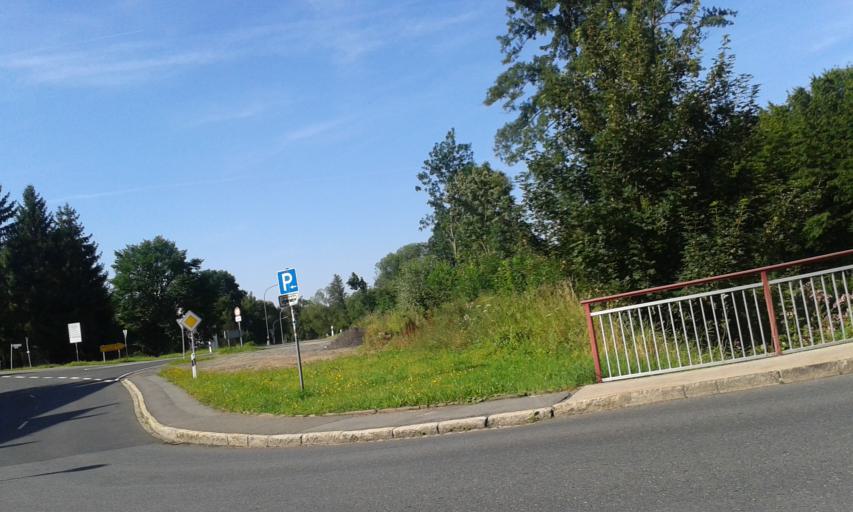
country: DE
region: Bavaria
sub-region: Upper Palatinate
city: Neustadt an der Waldnaab
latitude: 49.7273
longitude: 12.1681
